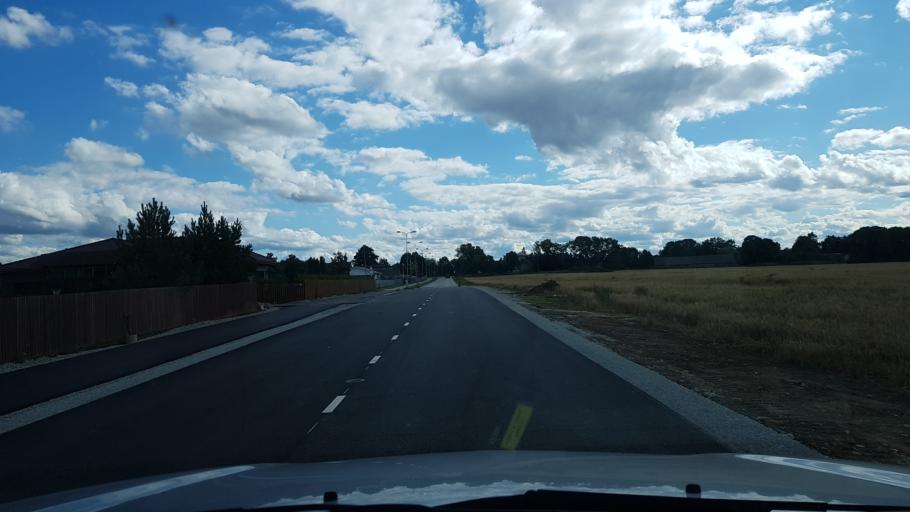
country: EE
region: Harju
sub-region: Rae vald
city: Jueri
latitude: 59.3763
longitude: 24.8321
